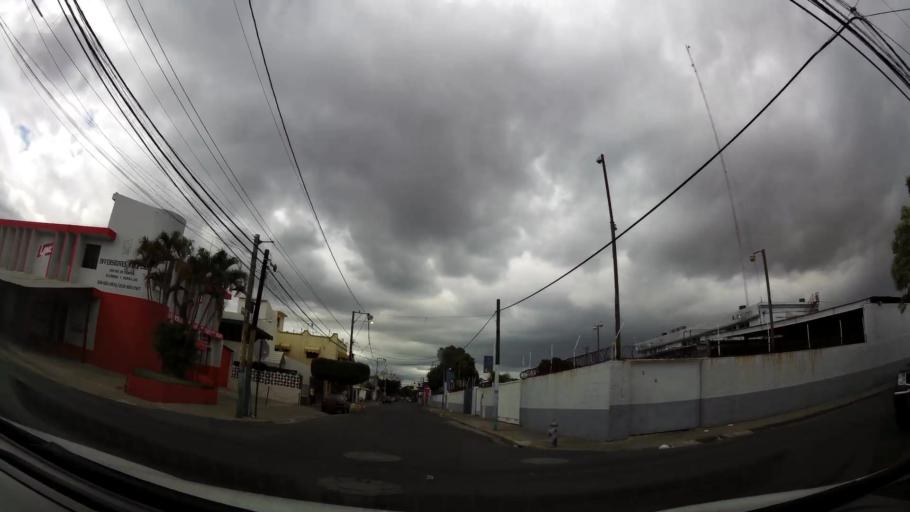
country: DO
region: Nacional
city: San Carlos
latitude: 18.4859
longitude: -69.9188
